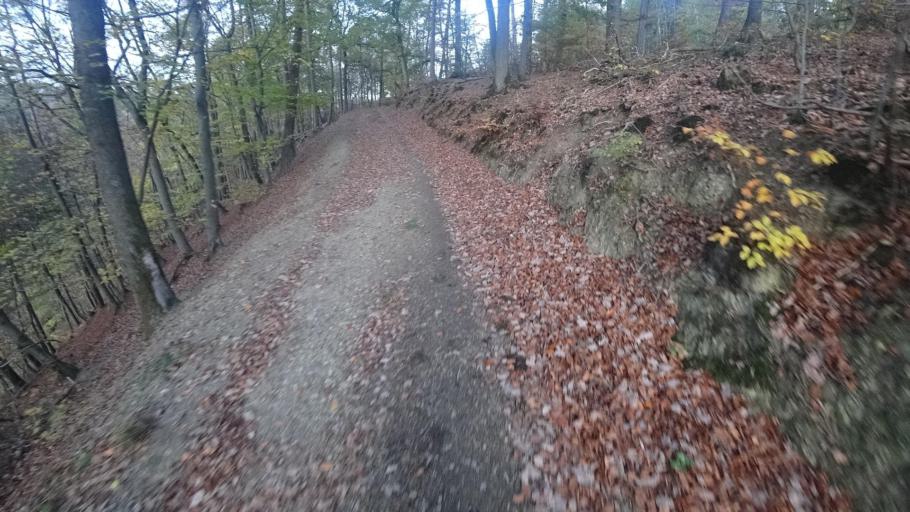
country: DE
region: Rheinland-Pfalz
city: Berg
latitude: 50.5309
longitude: 6.9469
